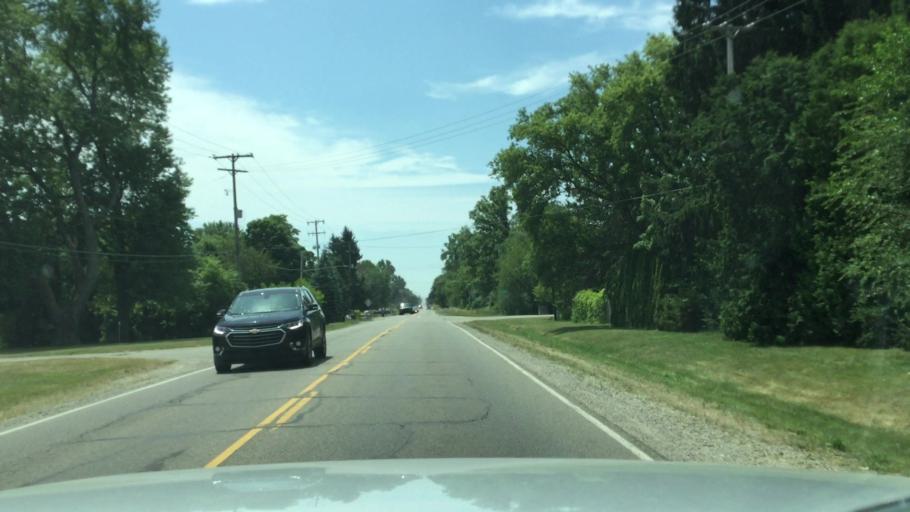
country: US
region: Michigan
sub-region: Genesee County
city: Swartz Creek
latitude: 43.0162
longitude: -83.7830
